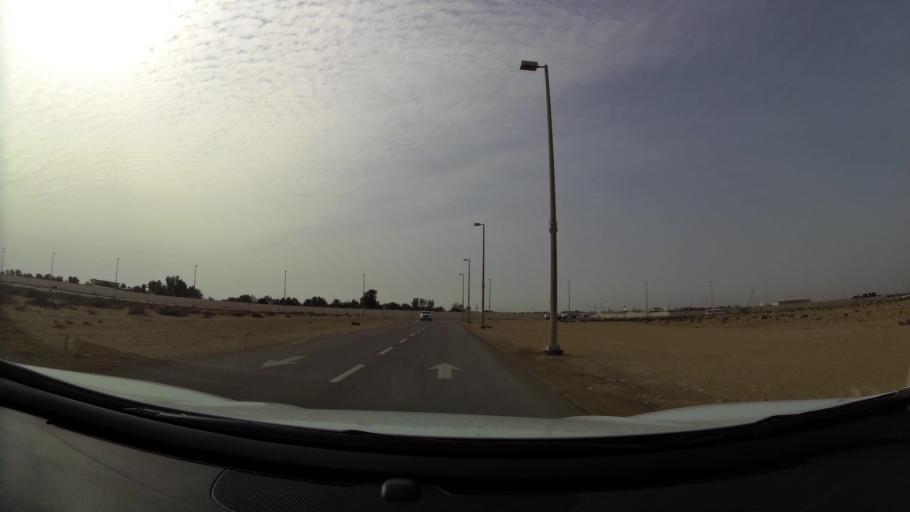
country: AE
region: Abu Dhabi
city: Abu Dhabi
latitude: 24.6214
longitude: 54.7097
